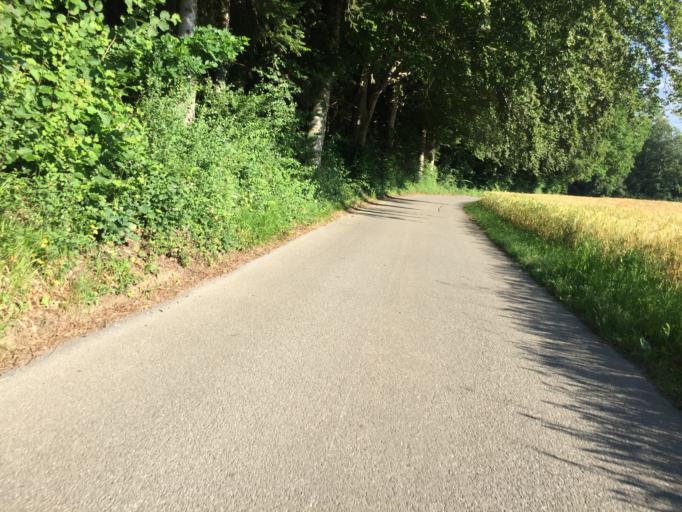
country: CH
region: Bern
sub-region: Bern-Mittelland District
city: Niederwichtrach
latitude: 46.8357
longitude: 7.5834
